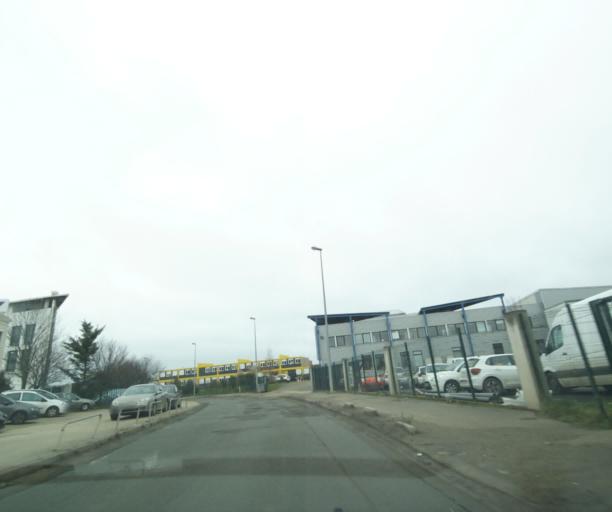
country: FR
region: Ile-de-France
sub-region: Departement du Val-de-Marne
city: Ablon-sur-Seine
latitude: 48.7321
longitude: 2.4316
